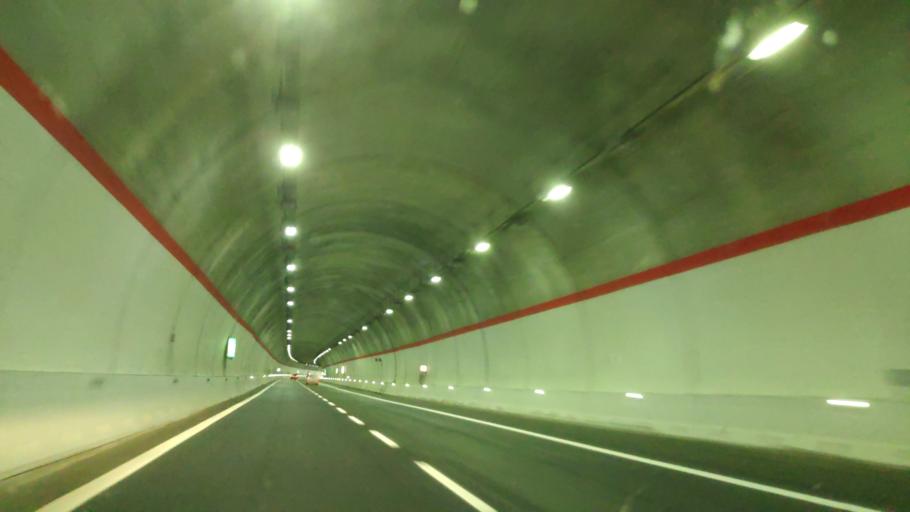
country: IT
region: Basilicate
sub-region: Provincia di Potenza
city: Lagonegro
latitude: 40.1115
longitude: 15.7906
